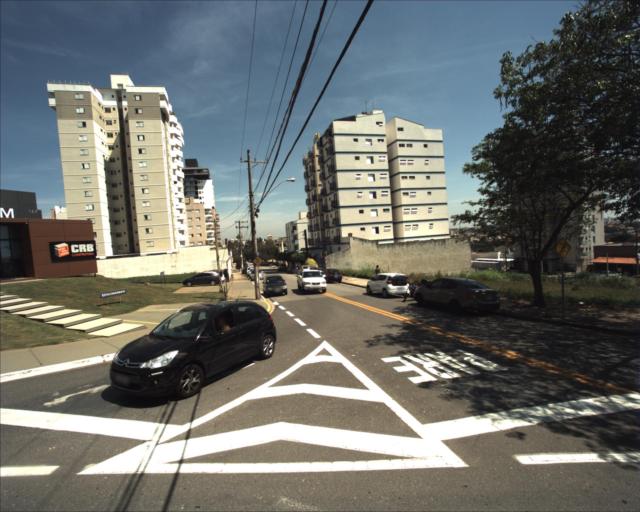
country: BR
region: Sao Paulo
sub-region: Sorocaba
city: Sorocaba
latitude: -23.5319
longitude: -47.4667
